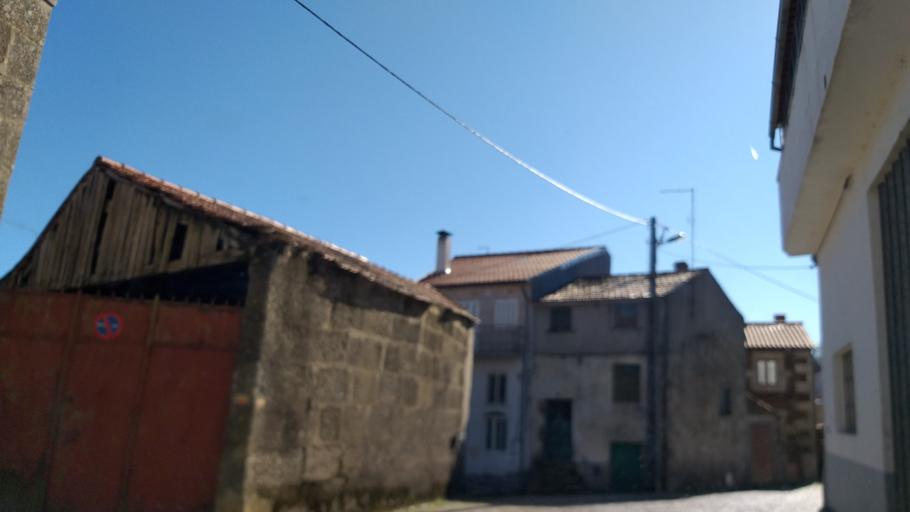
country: PT
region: Guarda
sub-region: Celorico da Beira
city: Celorico da Beira
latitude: 40.5143
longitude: -7.3921
